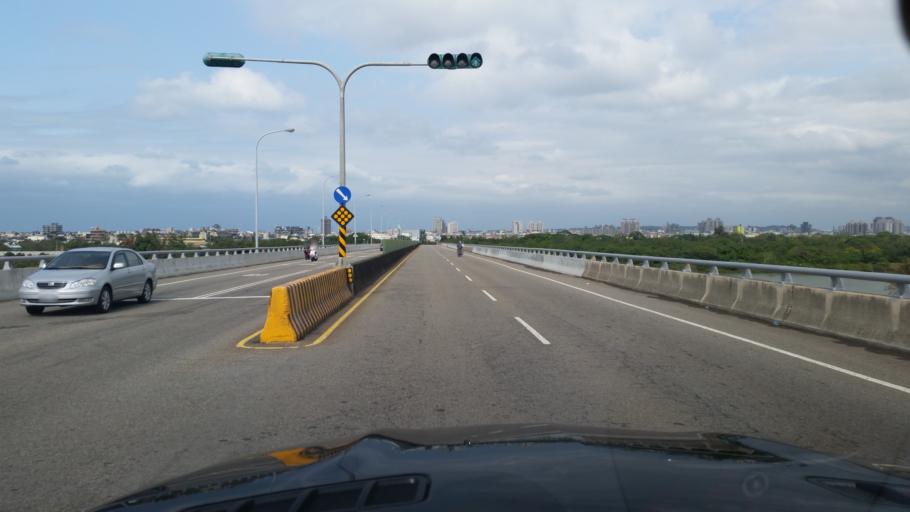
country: TW
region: Taiwan
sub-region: Miaoli
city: Miaoli
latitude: 24.6639
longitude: 120.8669
